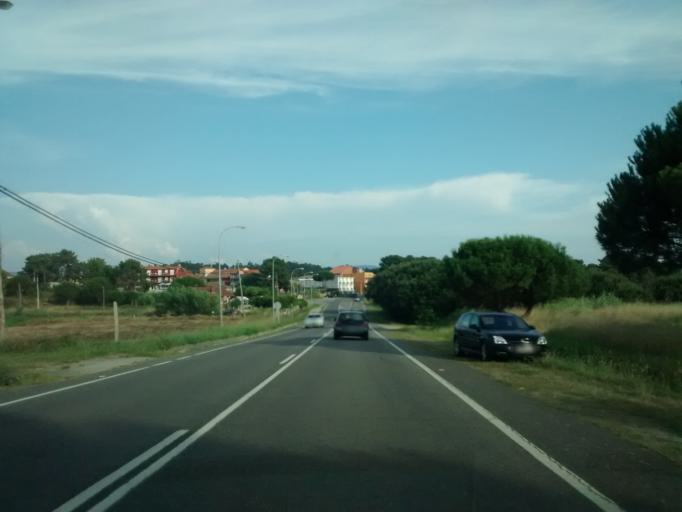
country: ES
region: Galicia
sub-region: Provincia de Pontevedra
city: Sanxenxo
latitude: 42.4001
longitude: -8.8471
